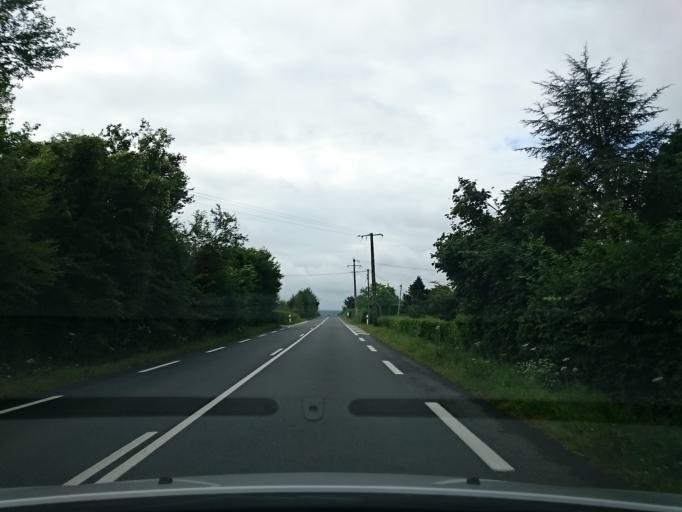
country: FR
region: Lower Normandy
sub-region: Departement du Calvados
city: Beuvillers
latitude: 49.0747
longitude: 0.3245
